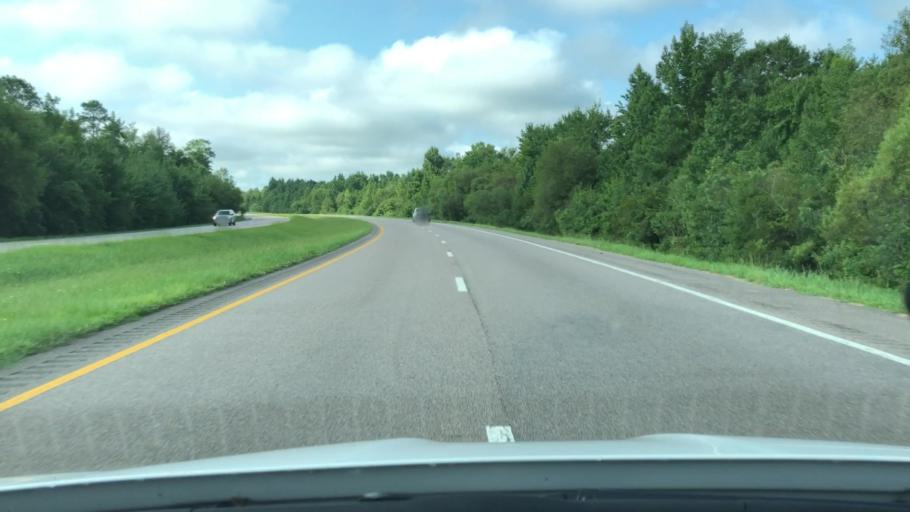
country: US
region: Virginia
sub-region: City of Portsmouth
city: Portsmouth Heights
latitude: 36.6691
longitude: -76.3545
